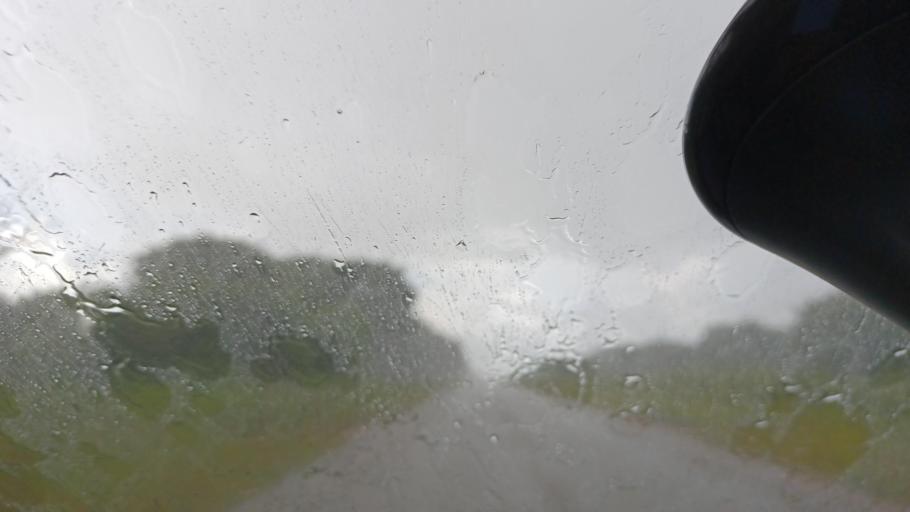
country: ZM
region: North-Western
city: Kasempa
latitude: -13.0936
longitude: 25.9195
